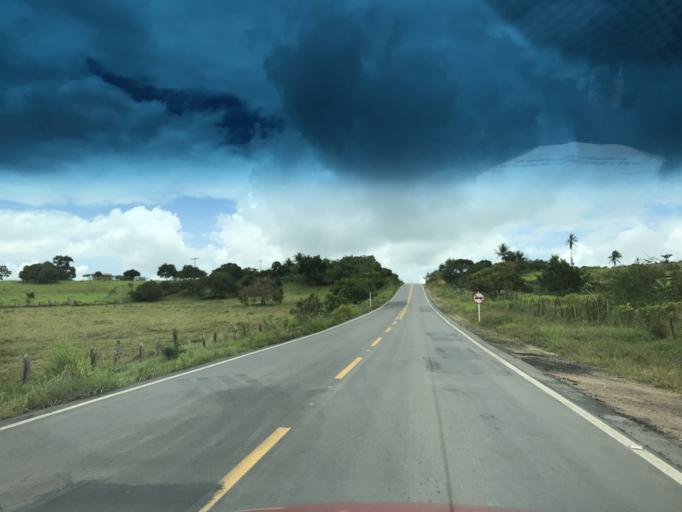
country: BR
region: Bahia
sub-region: Conceicao Do Almeida
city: Conceicao do Almeida
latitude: -12.6903
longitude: -39.2477
